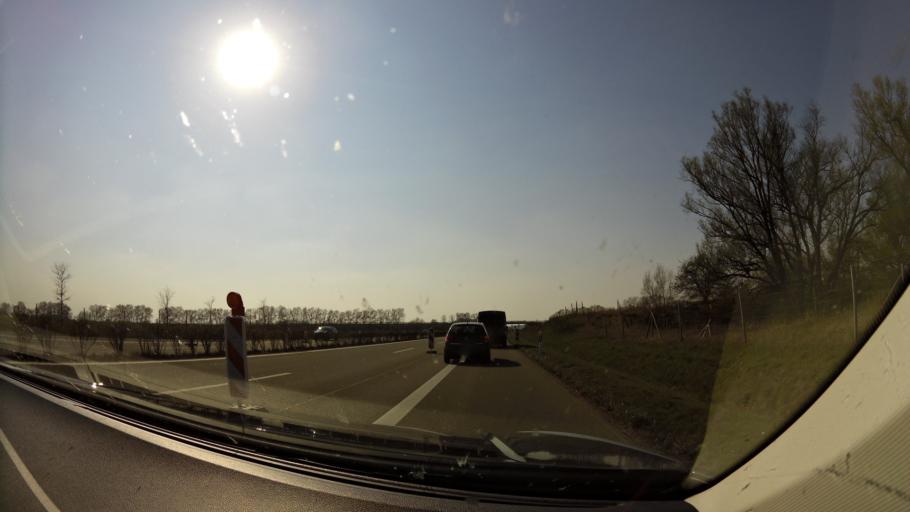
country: DE
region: Mecklenburg-Vorpommern
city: Franzburg
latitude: 54.0739
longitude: 12.9136
